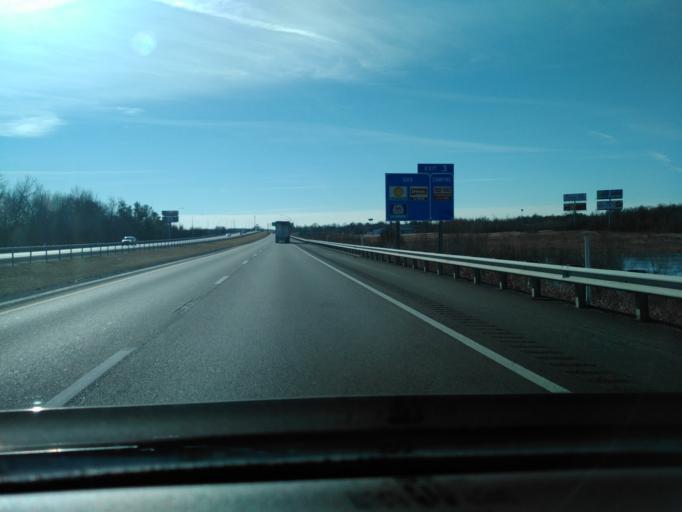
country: US
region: Illinois
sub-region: Massac County
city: Metropolis
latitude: 37.1052
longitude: -88.6911
